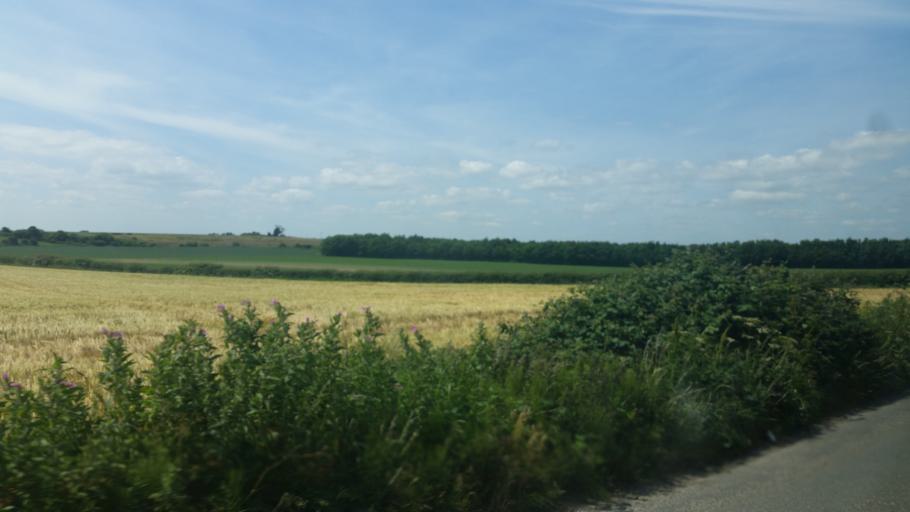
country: IE
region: Leinster
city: Lusk
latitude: 53.5347
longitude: -6.1791
